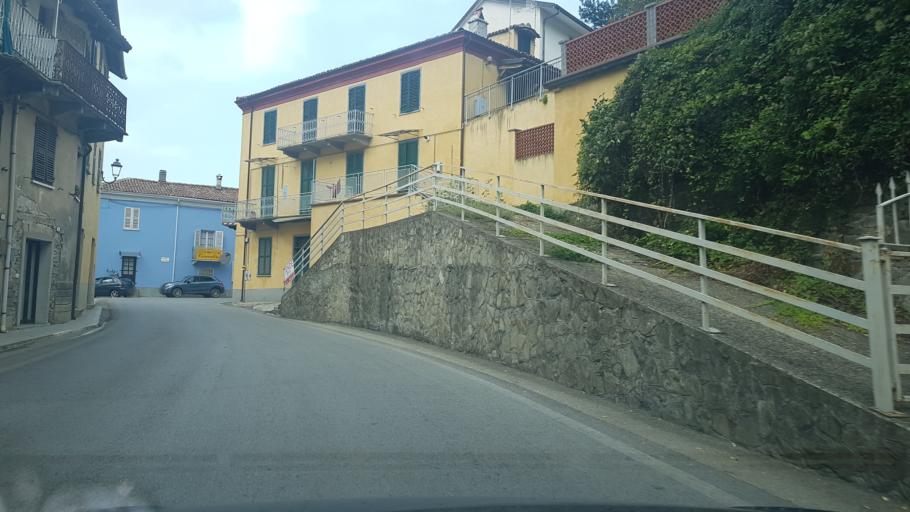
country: IT
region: Piedmont
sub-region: Provincia di Cuneo
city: Cossano Belbo
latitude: 44.6673
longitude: 8.1981
